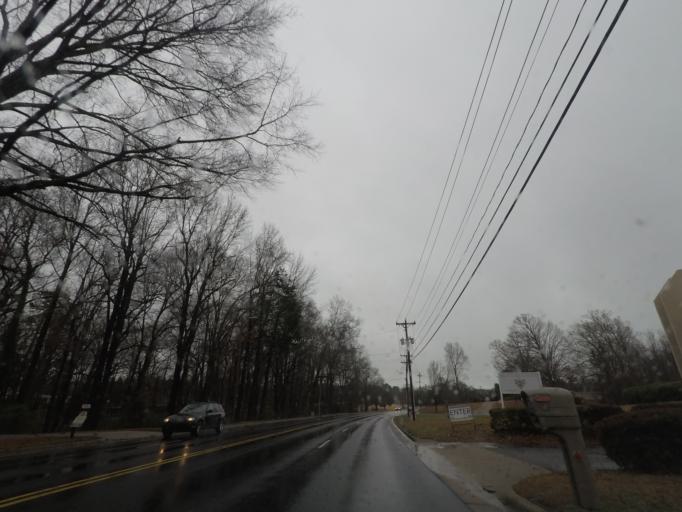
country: US
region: North Carolina
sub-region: Durham County
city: Durham
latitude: 36.0331
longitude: -78.9525
